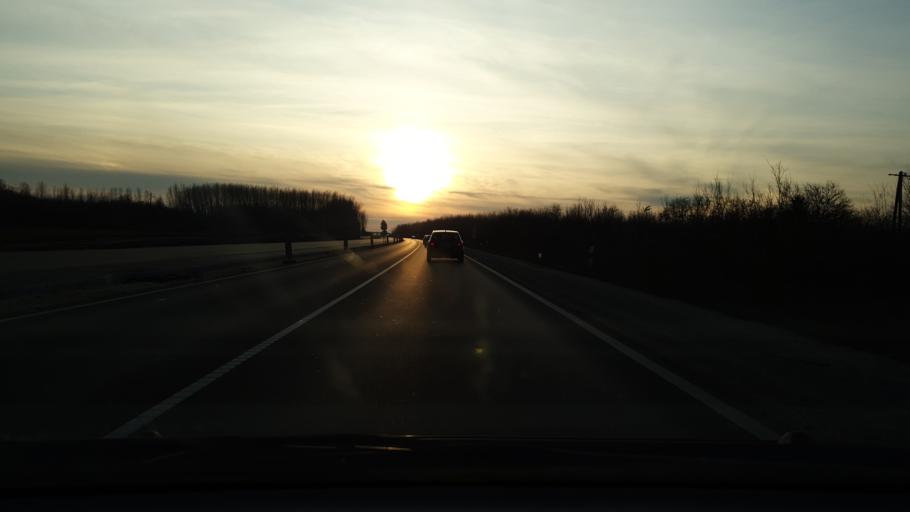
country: HU
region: Pest
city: Abony
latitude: 47.2141
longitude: 19.9736
